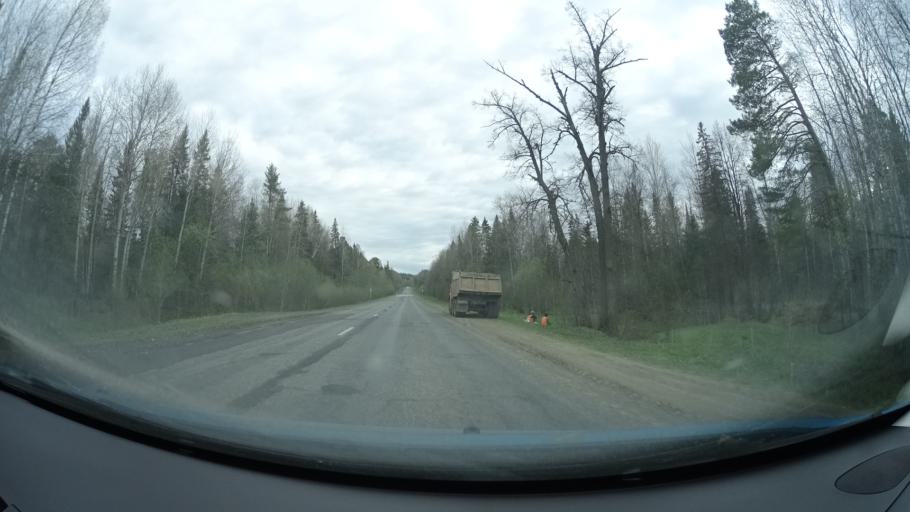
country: RU
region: Perm
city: Yugo-Kamskiy
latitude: 57.6396
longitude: 55.6091
